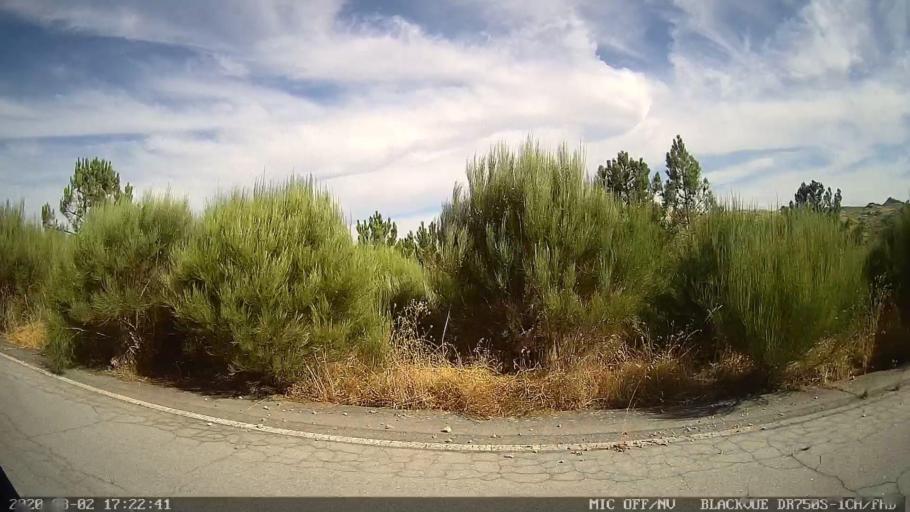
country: PT
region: Vila Real
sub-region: Sabrosa
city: Sabrosa
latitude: 41.3613
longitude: -7.5588
